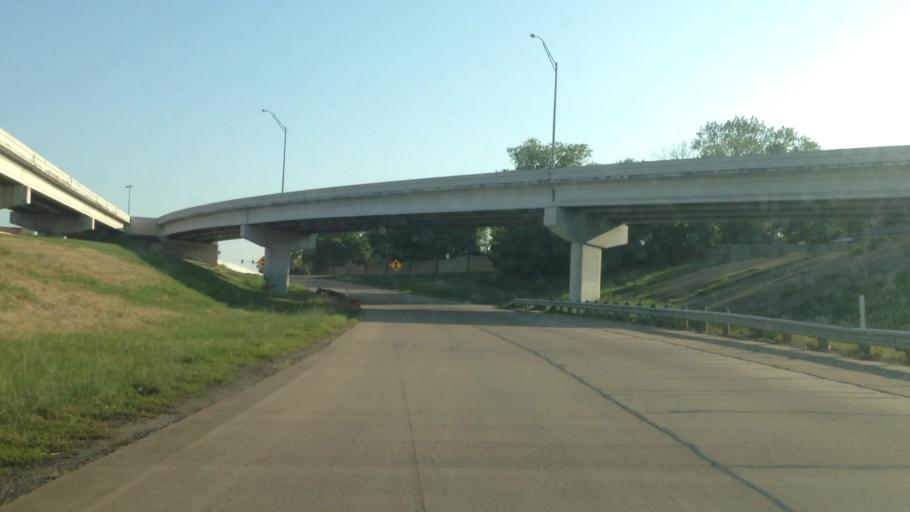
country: US
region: Texas
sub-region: Tarrant County
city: Richland Hills
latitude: 32.7576
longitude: -97.2157
